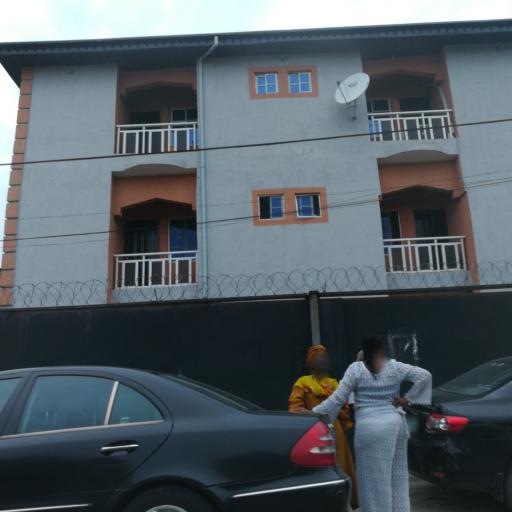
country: NG
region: Lagos
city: Makoko
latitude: 6.5028
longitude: 3.3785
